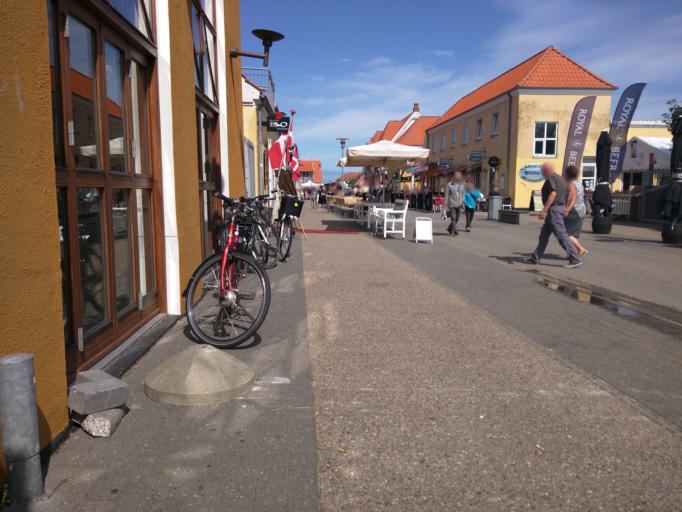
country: DK
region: North Denmark
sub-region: Frederikshavn Kommune
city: Skagen
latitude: 57.7212
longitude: 10.5894
